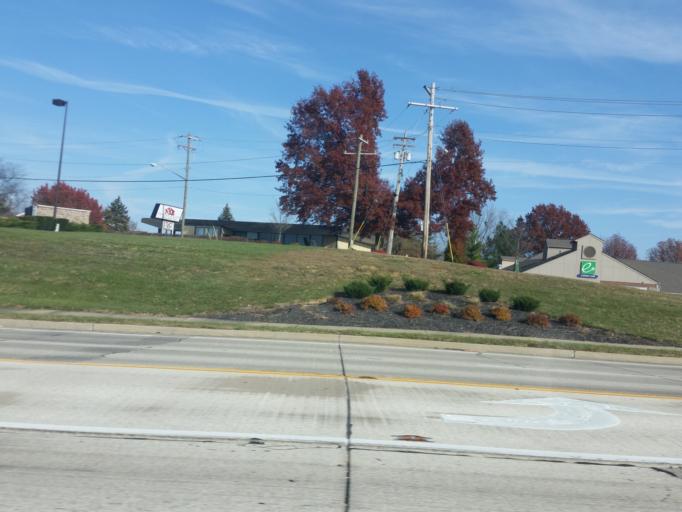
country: US
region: Kentucky
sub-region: Campbell County
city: Highland Heights
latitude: 39.0318
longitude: -84.4523
